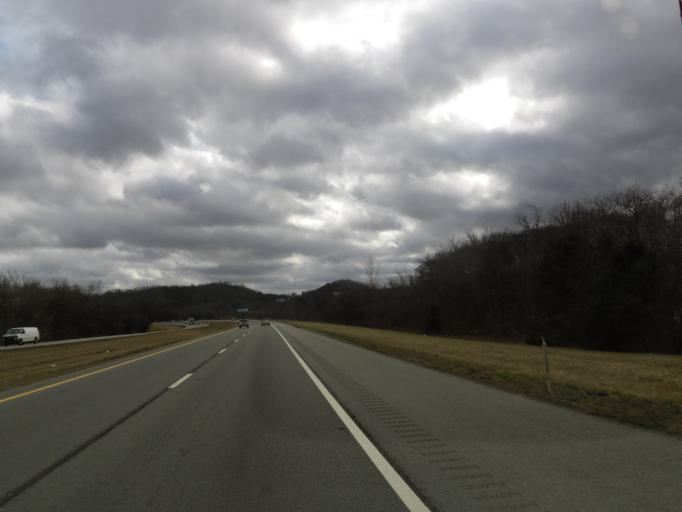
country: US
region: Tennessee
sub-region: Coffee County
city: New Union
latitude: 35.5740
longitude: -86.2317
